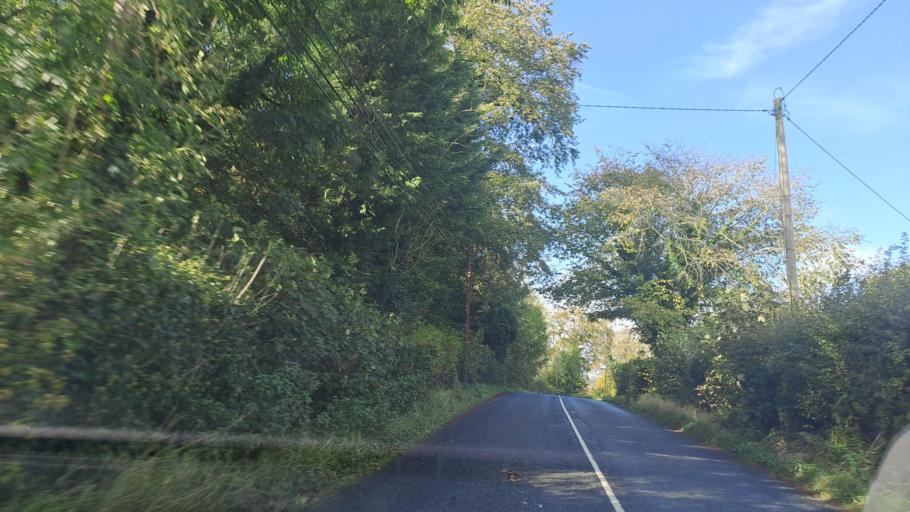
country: IE
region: Ulster
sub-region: An Cabhan
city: Bailieborough
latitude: 54.0057
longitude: -6.9174
